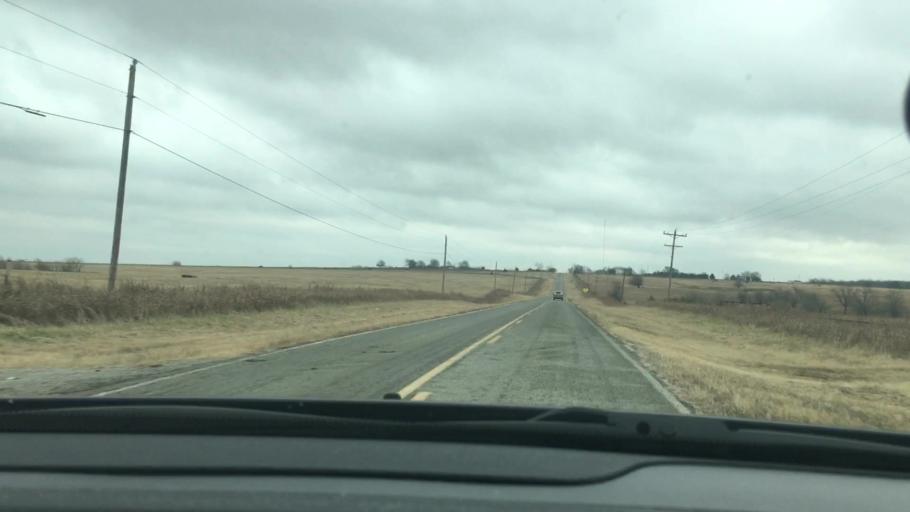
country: US
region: Oklahoma
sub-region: Johnston County
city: Tishomingo
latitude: 34.1433
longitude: -96.5141
